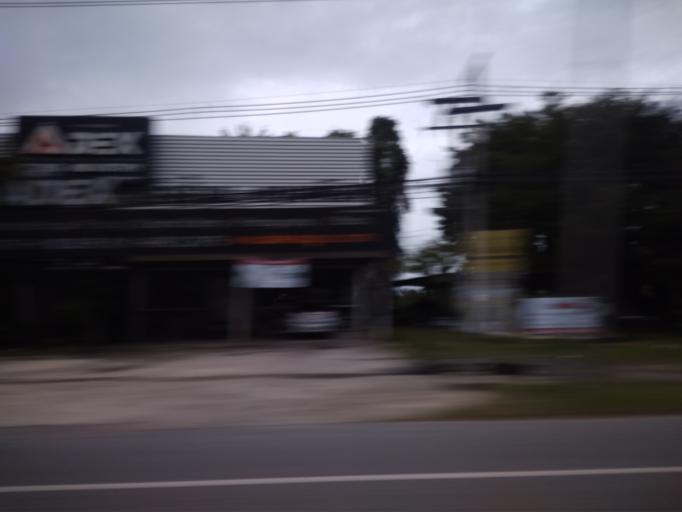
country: TH
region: Phuket
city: Ban Ko Kaeo
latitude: 7.9219
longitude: 98.3709
